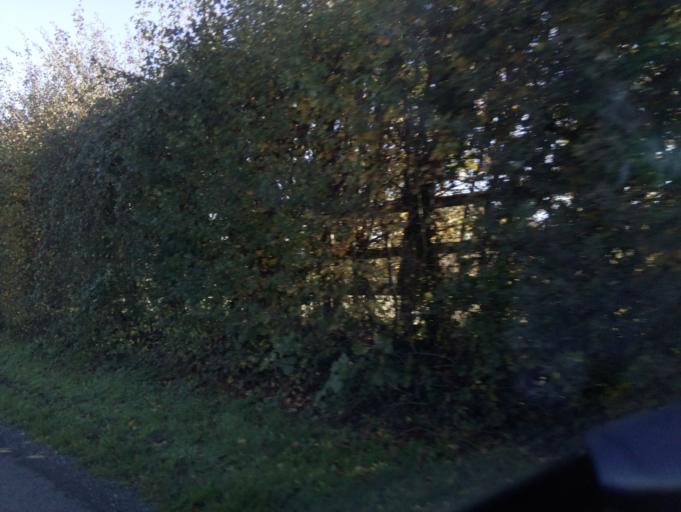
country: GB
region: England
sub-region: Somerset
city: Yeovil
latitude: 50.9210
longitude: -2.6163
